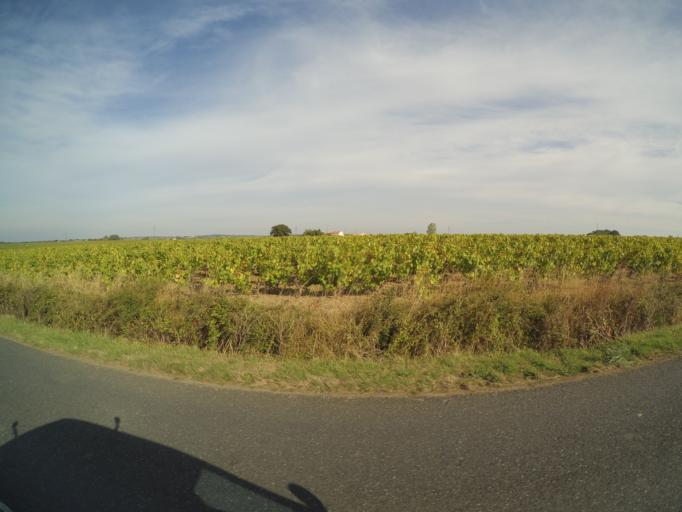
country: FR
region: Pays de la Loire
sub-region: Departement de la Loire-Atlantique
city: Mouzillon
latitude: 47.1258
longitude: -1.2419
